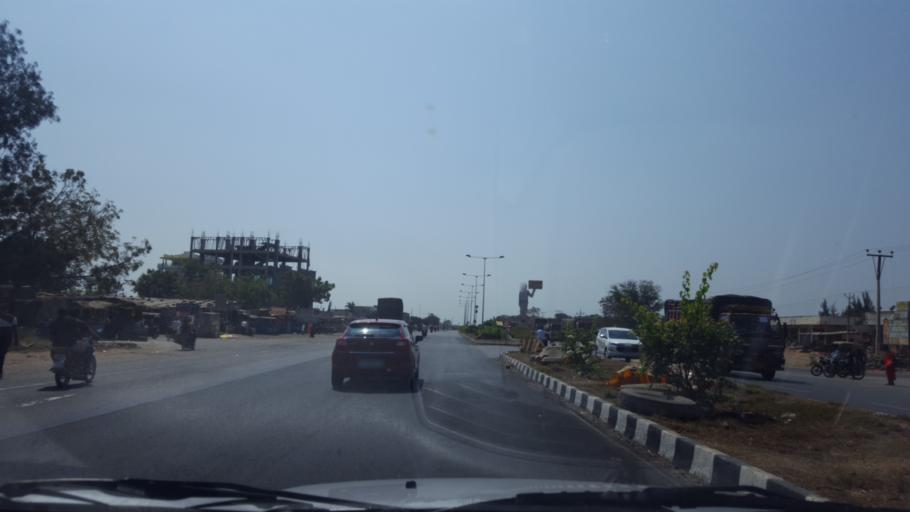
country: IN
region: Andhra Pradesh
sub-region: Prakasam
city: Addanki
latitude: 15.6868
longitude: 80.0182
